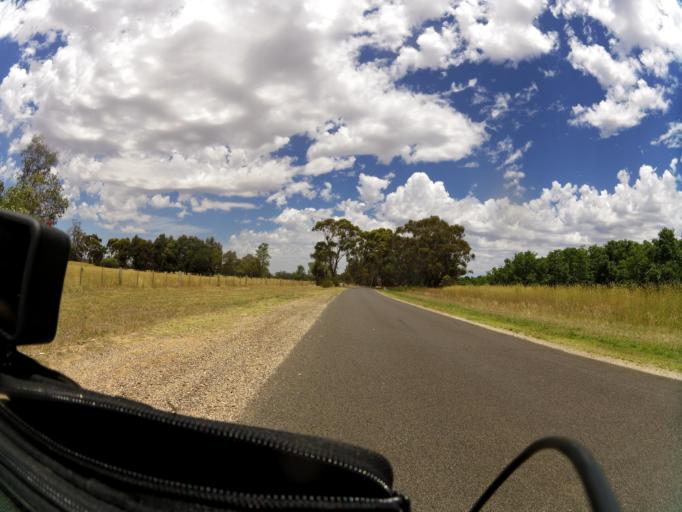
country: AU
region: Victoria
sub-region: Greater Shepparton
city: Shepparton
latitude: -36.6963
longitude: 145.1729
